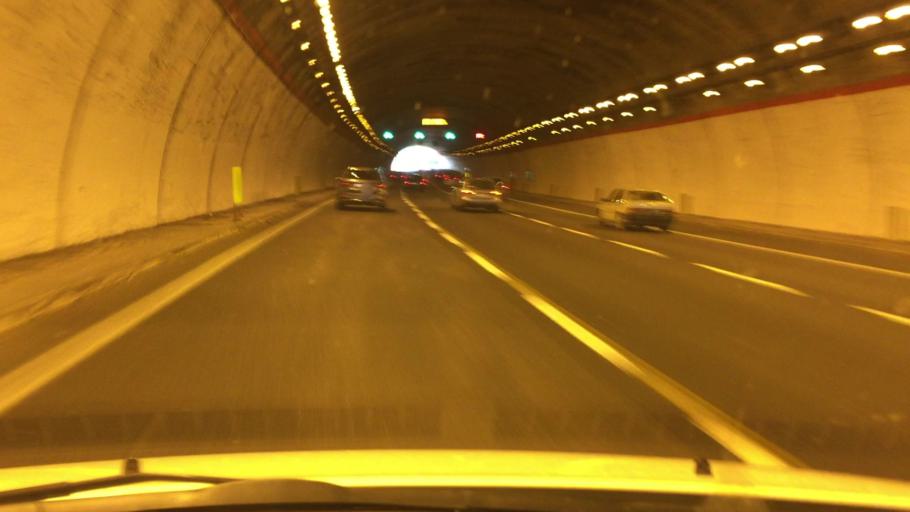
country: VA
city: Vatican City
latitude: 41.9703
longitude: 12.4086
